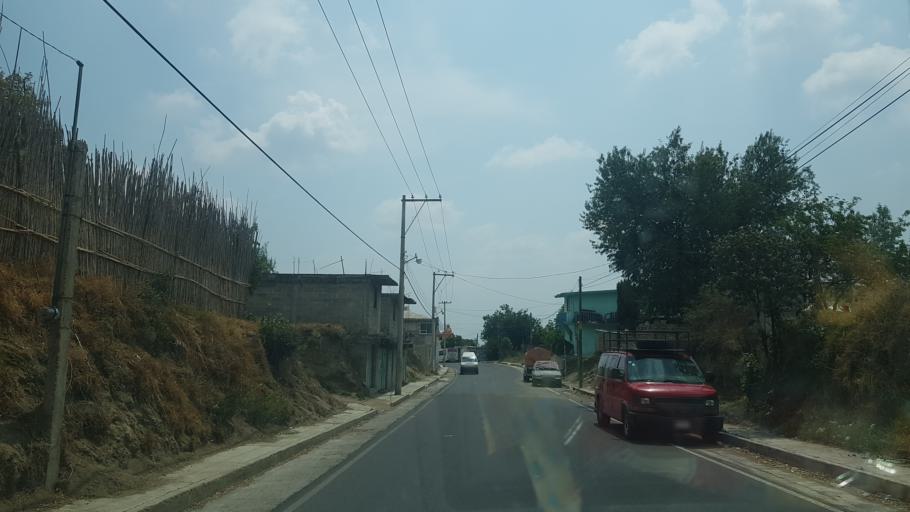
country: MX
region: Puebla
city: Domingo Arenas
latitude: 19.1405
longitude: -98.4636
